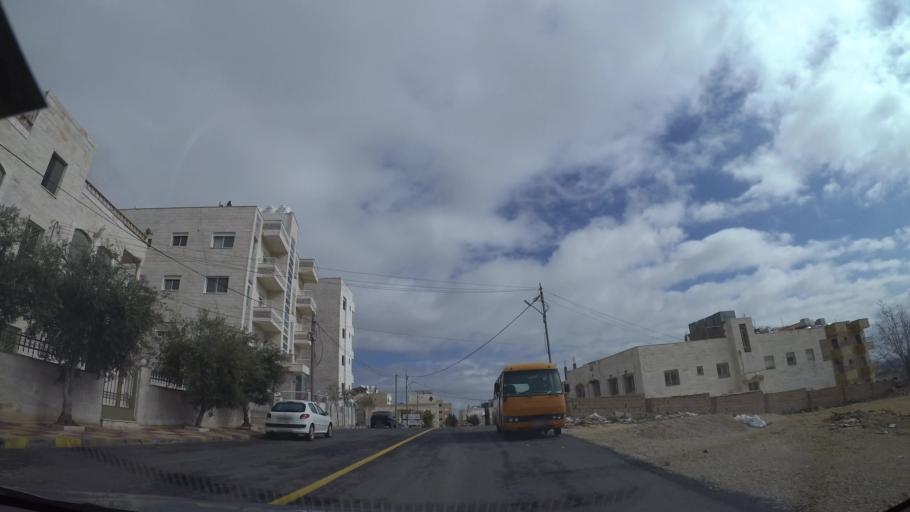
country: JO
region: Amman
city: Al Jubayhah
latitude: 32.0569
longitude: 35.8887
